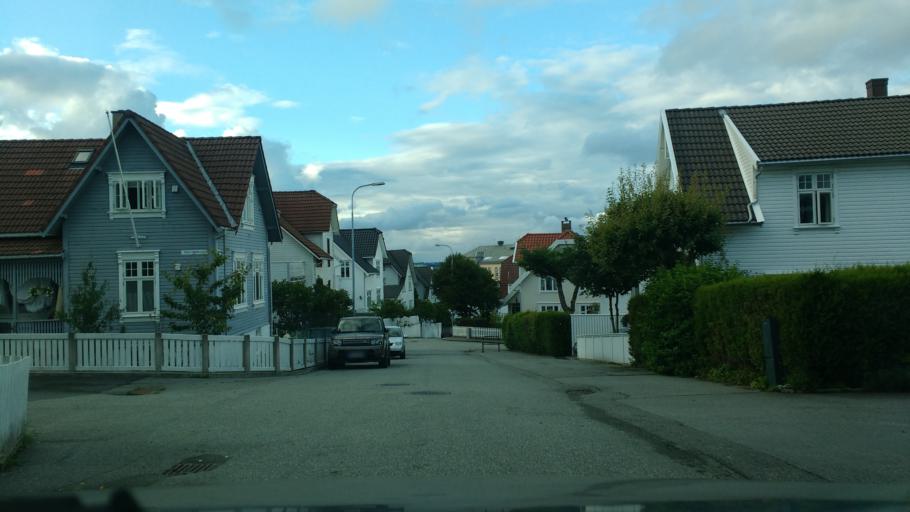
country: NO
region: Rogaland
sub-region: Stavanger
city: Stavanger
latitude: 58.9599
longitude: 5.7317
